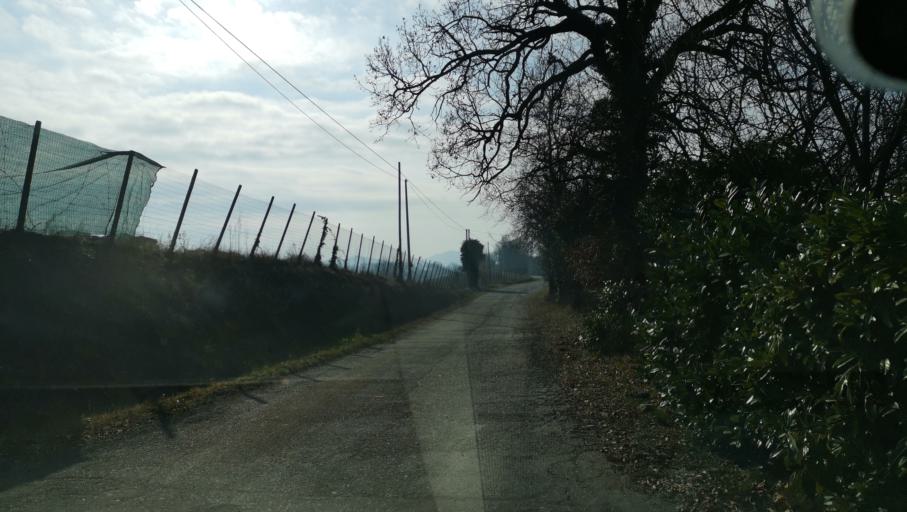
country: IT
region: Piedmont
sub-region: Provincia di Torino
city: Rivalba
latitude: 45.1296
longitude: 7.8962
